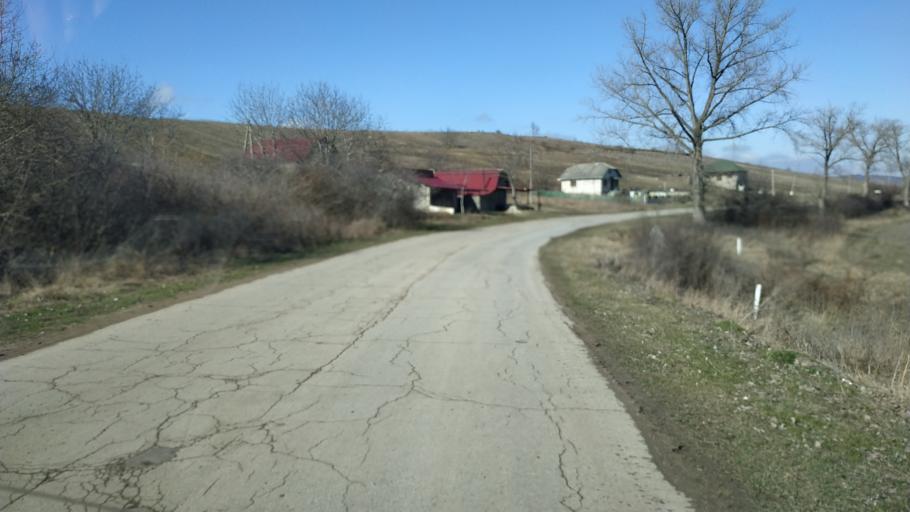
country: MD
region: Hincesti
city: Hincesti
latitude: 46.9772
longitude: 28.5707
